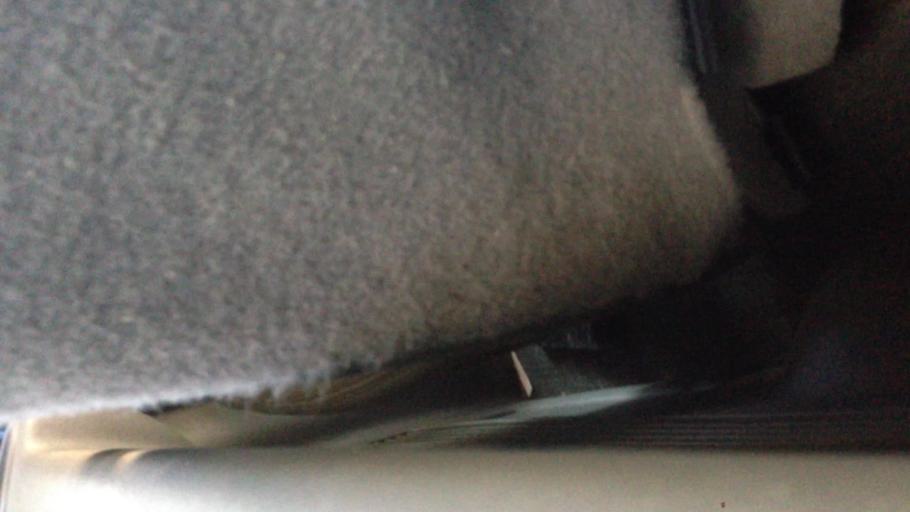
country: US
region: New York
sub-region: Dutchess County
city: Tivoli
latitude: 42.1082
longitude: -73.8187
